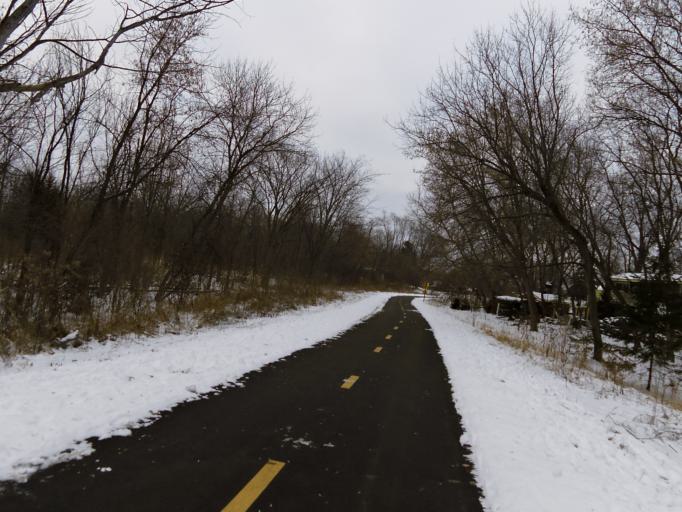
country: US
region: Minnesota
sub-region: Scott County
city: Prior Lake
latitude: 44.7075
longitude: -93.4668
